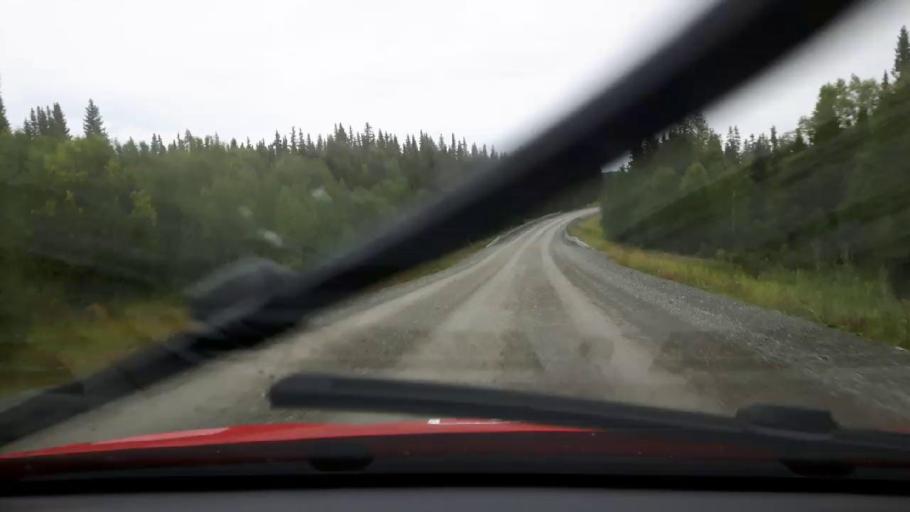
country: SE
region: Jaemtland
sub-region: Are Kommun
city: Are
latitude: 63.4709
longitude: 12.5930
